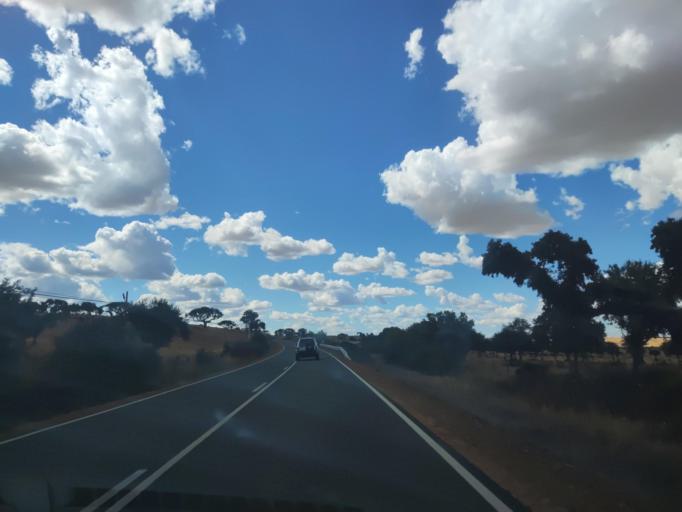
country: ES
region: Castille and Leon
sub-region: Provincia de Salamanca
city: Tamames
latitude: 40.6506
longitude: -6.0791
